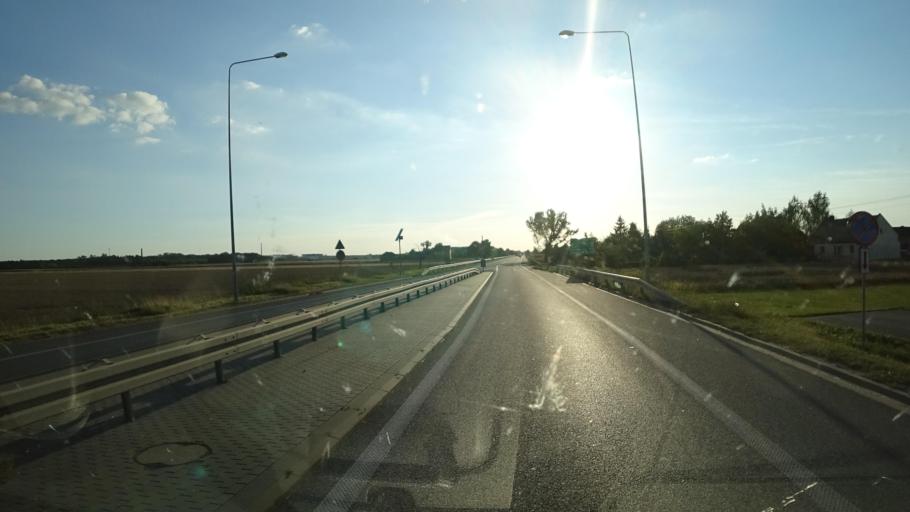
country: PL
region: Lodz Voivodeship
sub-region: Powiat kutnowski
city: Krzyzanow
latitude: 52.2202
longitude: 19.4601
